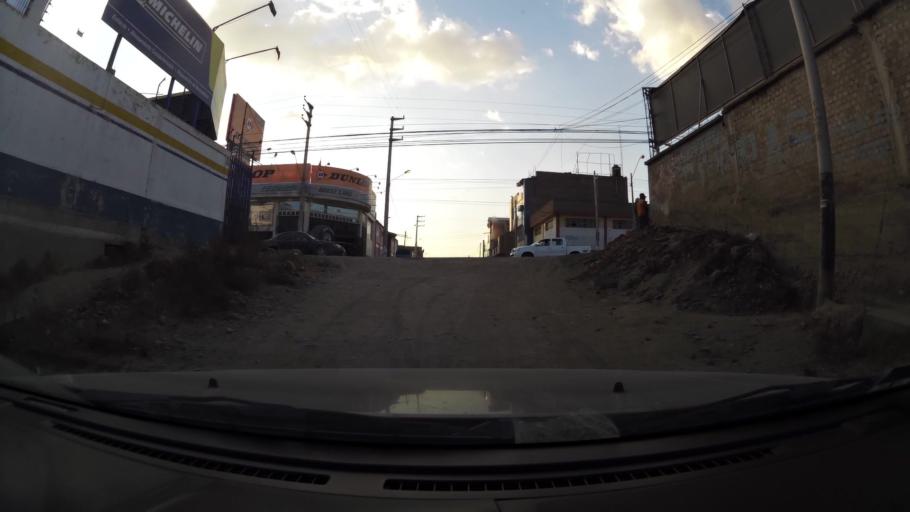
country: PE
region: Junin
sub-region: Provincia de Huancayo
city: Pilcomay
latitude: -12.0442
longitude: -75.2267
